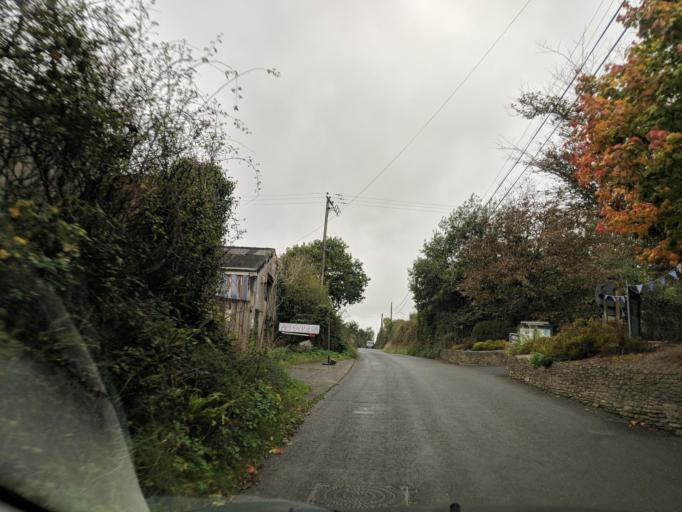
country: GB
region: England
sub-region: Cornwall
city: Saltash
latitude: 50.4419
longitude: -4.2110
